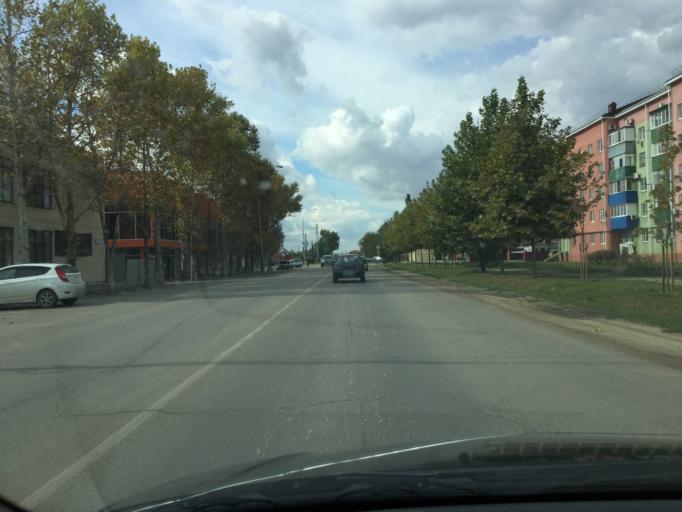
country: RU
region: Krasnodarskiy
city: Slavyansk-na-Kubani
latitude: 45.2509
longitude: 38.1042
